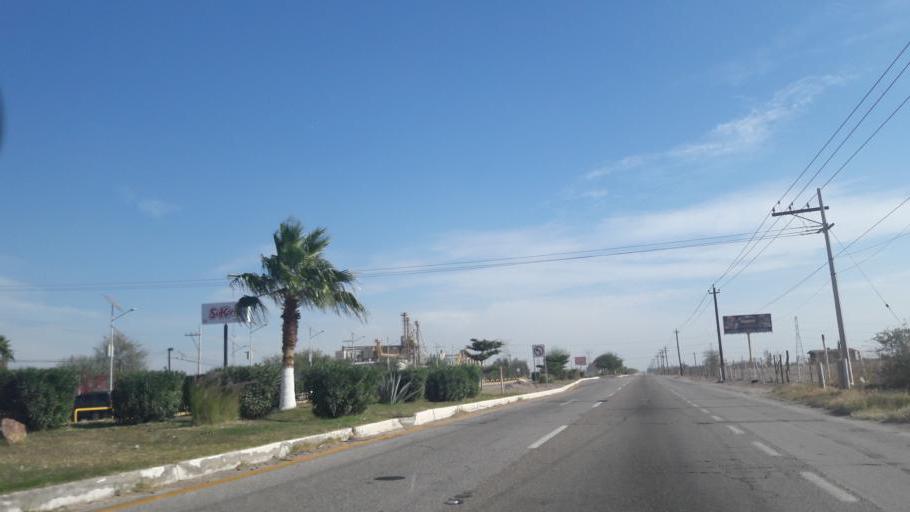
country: MX
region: Baja California
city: Progreso
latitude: 32.5990
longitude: -115.6458
